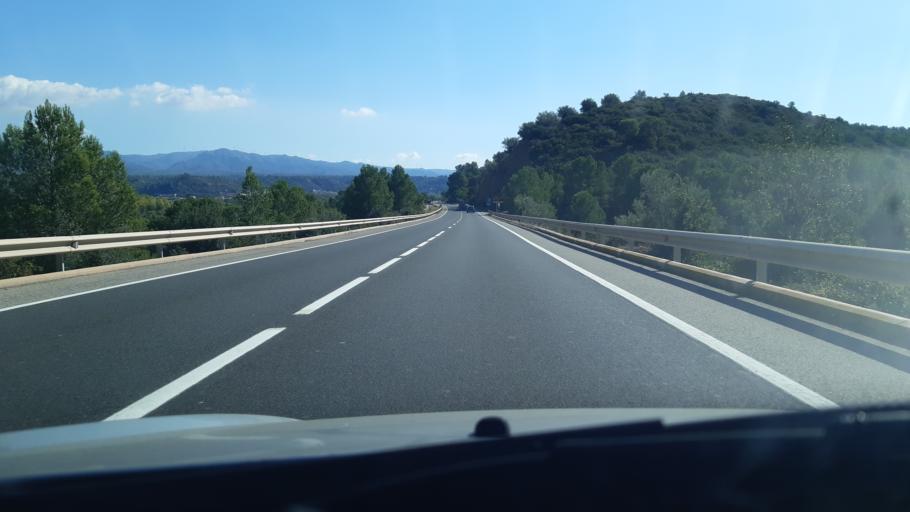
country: ES
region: Catalonia
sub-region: Provincia de Tarragona
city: Tivenys
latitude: 40.9242
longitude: 0.4884
